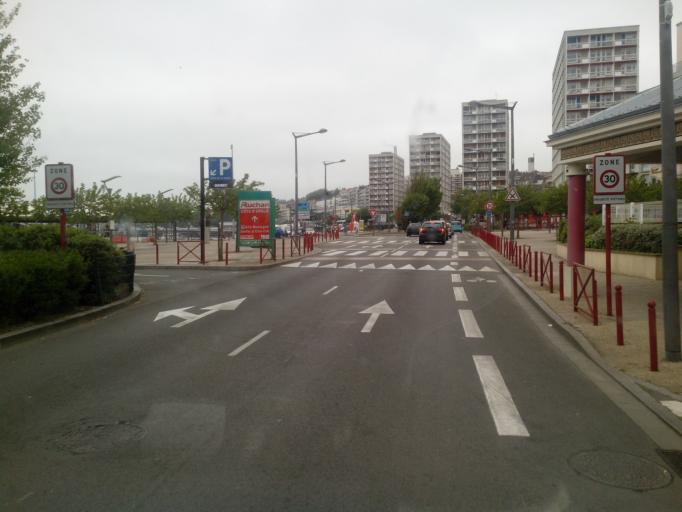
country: FR
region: Nord-Pas-de-Calais
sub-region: Departement du Pas-de-Calais
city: Boulogne-sur-Mer
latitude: 50.7229
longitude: 1.6020
